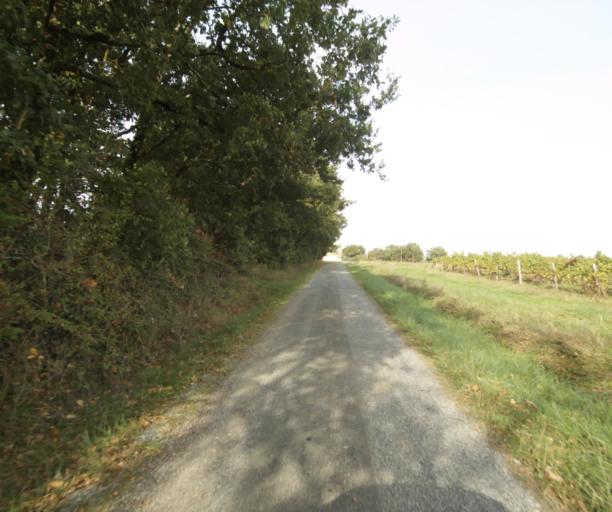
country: FR
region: Midi-Pyrenees
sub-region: Departement du Tarn-et-Garonne
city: Campsas
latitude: 43.9235
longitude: 1.3253
